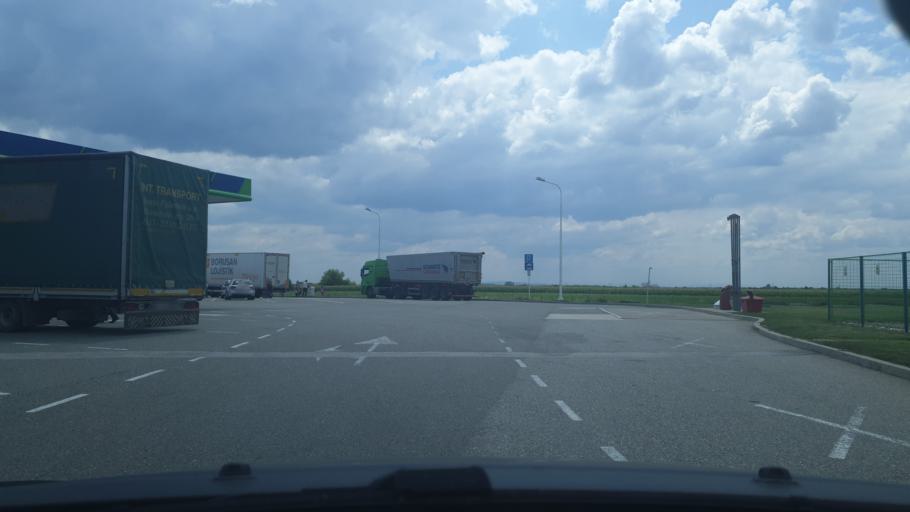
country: RS
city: Ravnje
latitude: 45.0358
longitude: 19.4490
